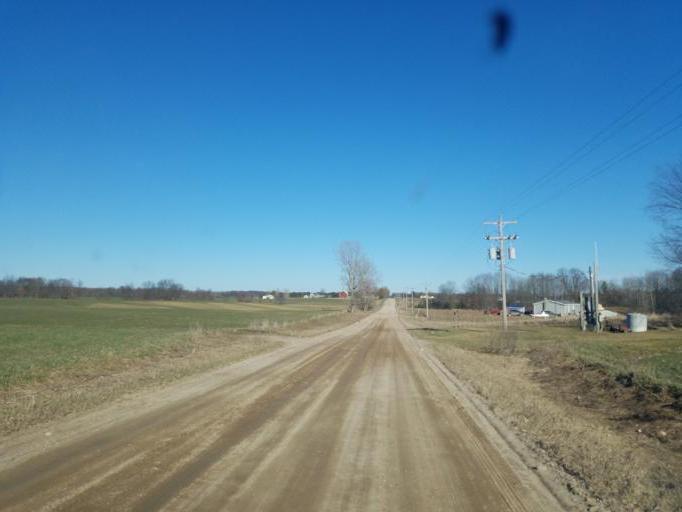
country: US
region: Michigan
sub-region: Montcalm County
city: Edmore
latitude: 43.4877
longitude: -85.0557
